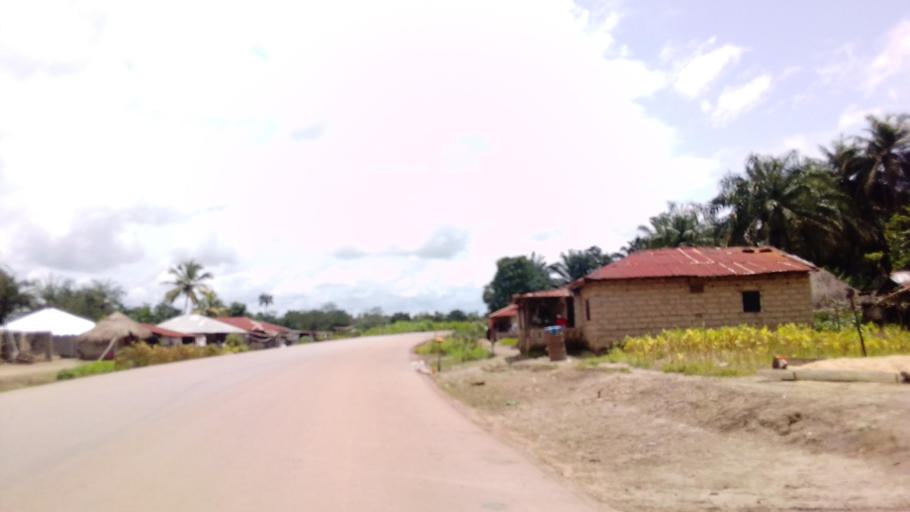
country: SL
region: Northern Province
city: Makeni
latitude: 9.0691
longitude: -12.1771
